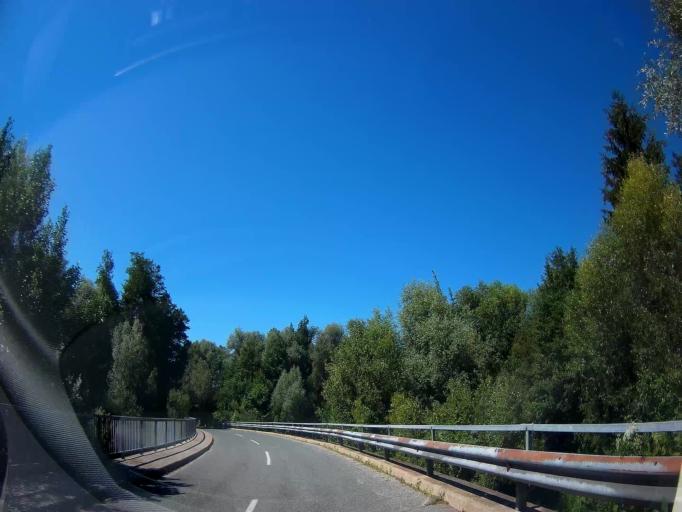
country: AT
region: Carinthia
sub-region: Politischer Bezirk Klagenfurt Land
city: Grafenstein
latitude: 46.6050
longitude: 14.4425
